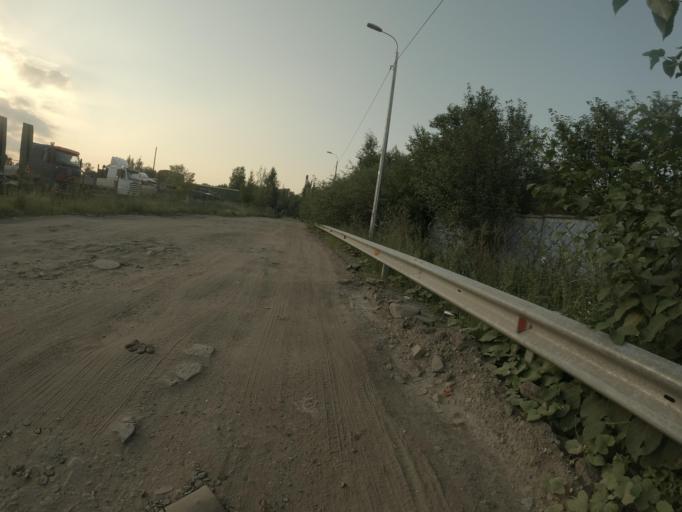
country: RU
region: St.-Petersburg
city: Krasnogvargeisky
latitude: 59.9574
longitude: 30.4568
